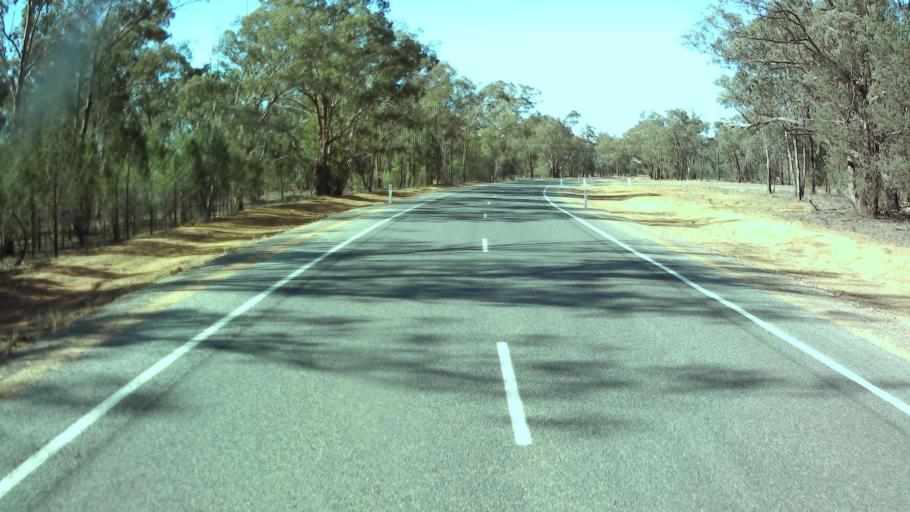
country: AU
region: New South Wales
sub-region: Weddin
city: Grenfell
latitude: -33.7555
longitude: 148.0827
